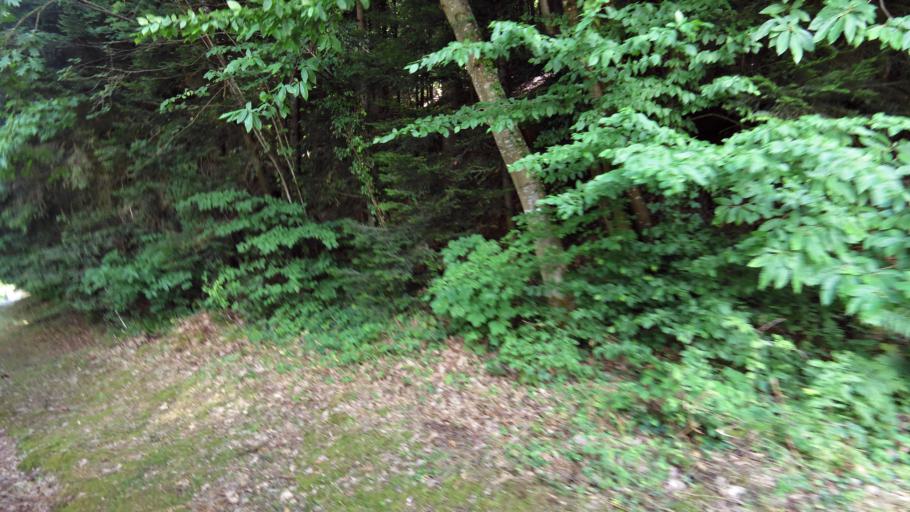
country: FR
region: Lorraine
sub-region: Departement de la Moselle
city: Abreschviller
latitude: 48.6318
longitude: 7.1008
